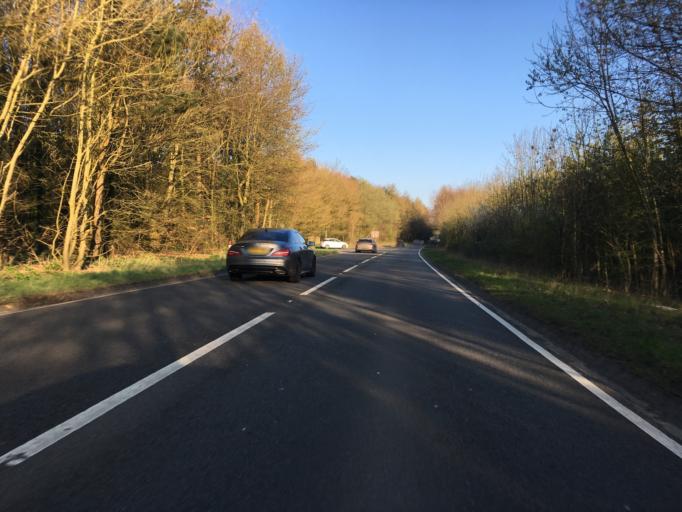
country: GB
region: England
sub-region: Gloucestershire
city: Northleach
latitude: 51.8274
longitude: -1.8086
